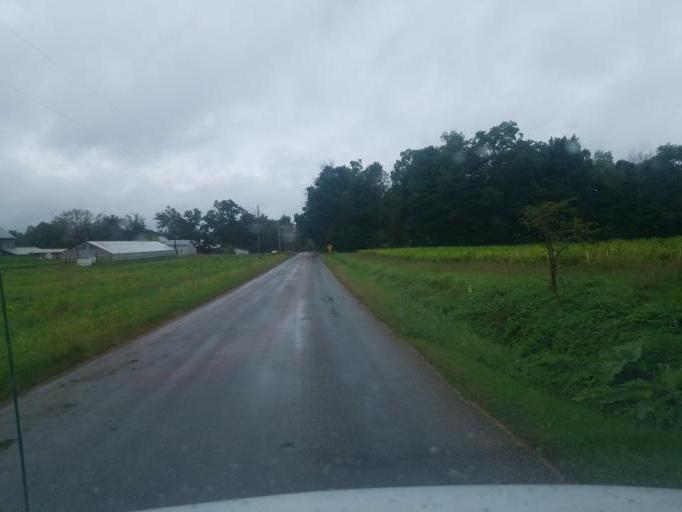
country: US
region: Ohio
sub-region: Wayne County
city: West Salem
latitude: 40.9475
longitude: -82.1190
